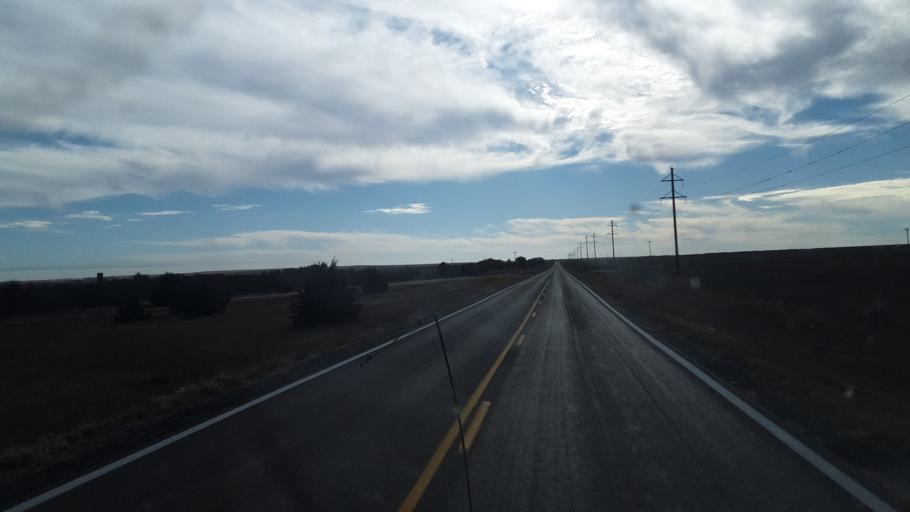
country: US
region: Kansas
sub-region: Hodgeman County
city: Jetmore
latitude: 38.1108
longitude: -99.7315
